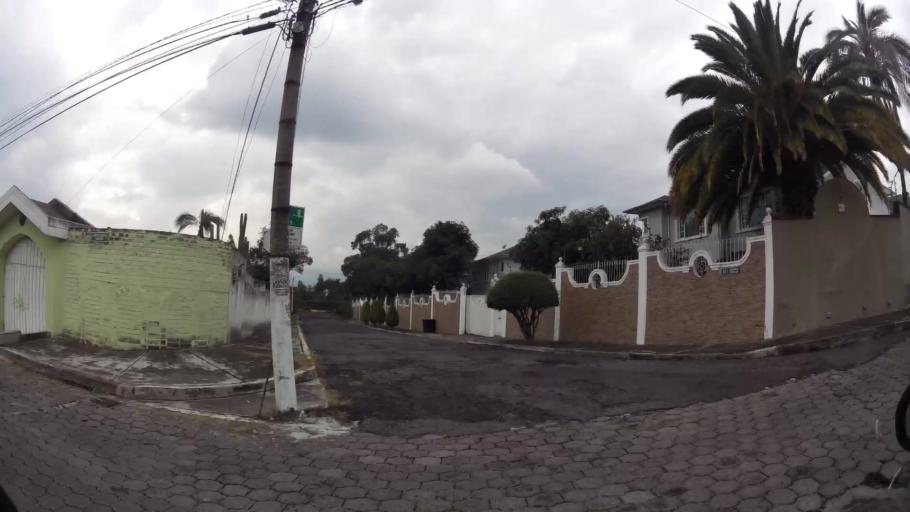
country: EC
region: Pichincha
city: Sangolqui
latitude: -0.3032
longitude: -78.4715
